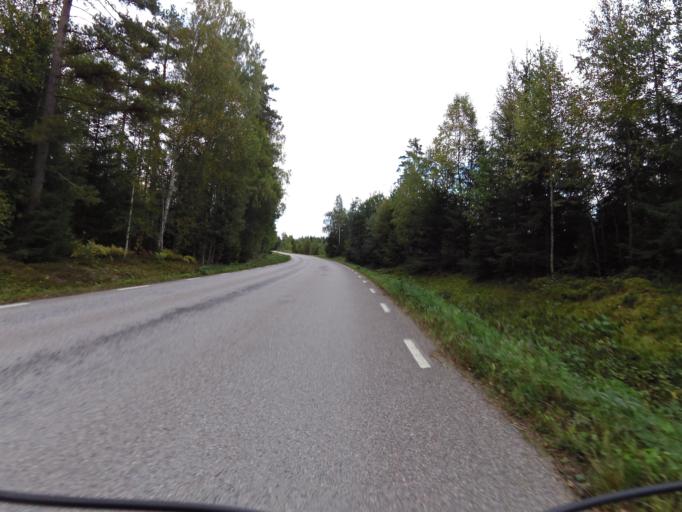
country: SE
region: Gaevleborg
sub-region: Sandvikens Kommun
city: Sandviken
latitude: 60.6486
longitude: 16.8212
